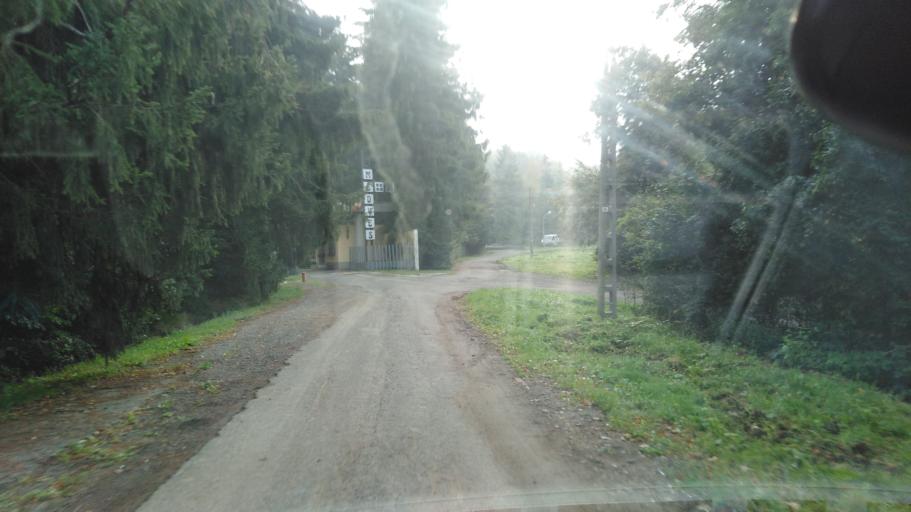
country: HU
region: Nograd
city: Somoskoujfalu
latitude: 48.1439
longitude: 19.8680
